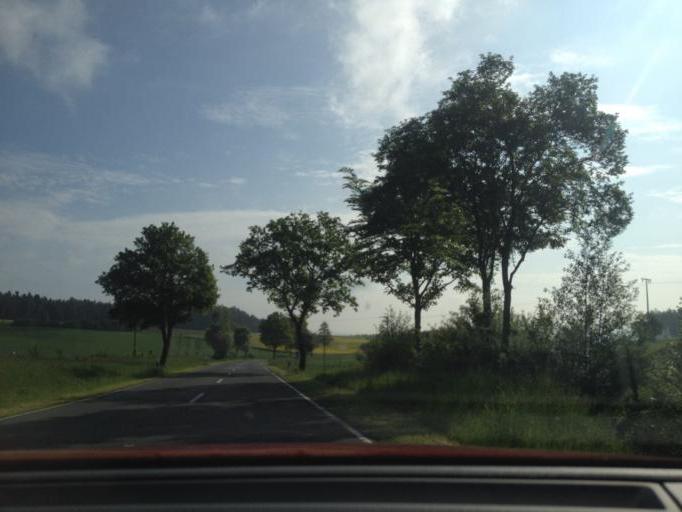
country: DE
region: Bavaria
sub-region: Upper Palatinate
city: Speinshart
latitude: 49.8005
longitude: 11.8495
